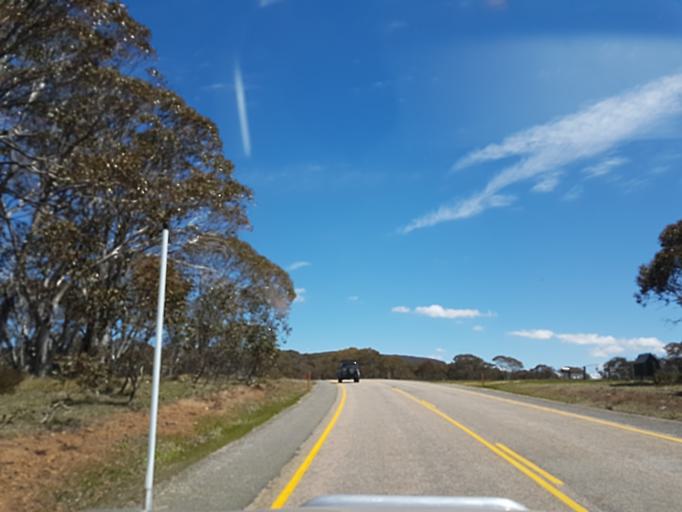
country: AU
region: Victoria
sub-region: Alpine
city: Mount Beauty
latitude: -37.0278
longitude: 147.2876
